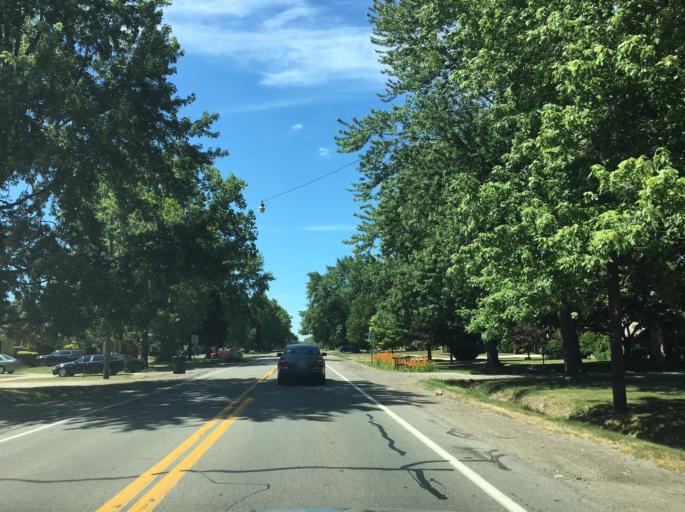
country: US
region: Michigan
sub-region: Wayne County
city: Allen Park
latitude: 42.2409
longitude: -83.2230
